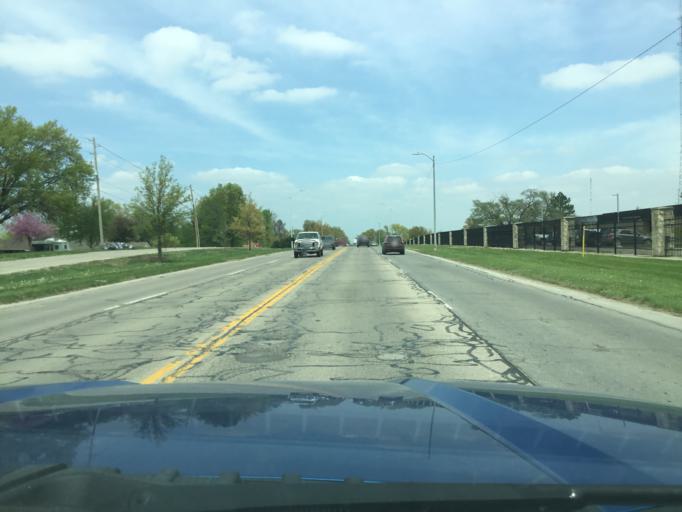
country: US
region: Kansas
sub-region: Shawnee County
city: Topeka
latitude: 39.0193
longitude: -95.6864
